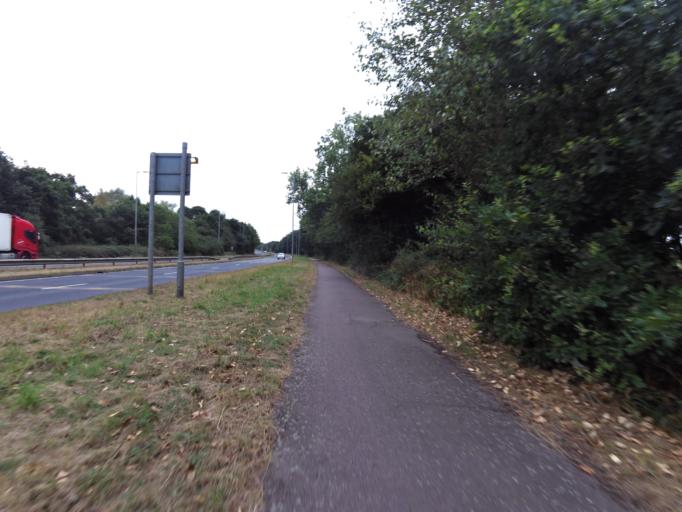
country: GB
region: England
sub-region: Hertfordshire
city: Shenley AV
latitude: 51.7407
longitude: -0.2742
